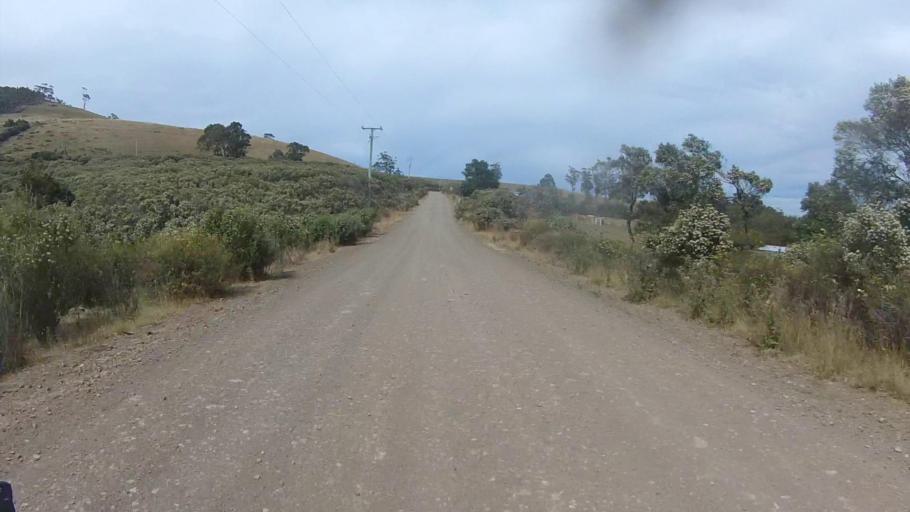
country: AU
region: Tasmania
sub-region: Sorell
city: Sorell
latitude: -42.7750
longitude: 147.8290
